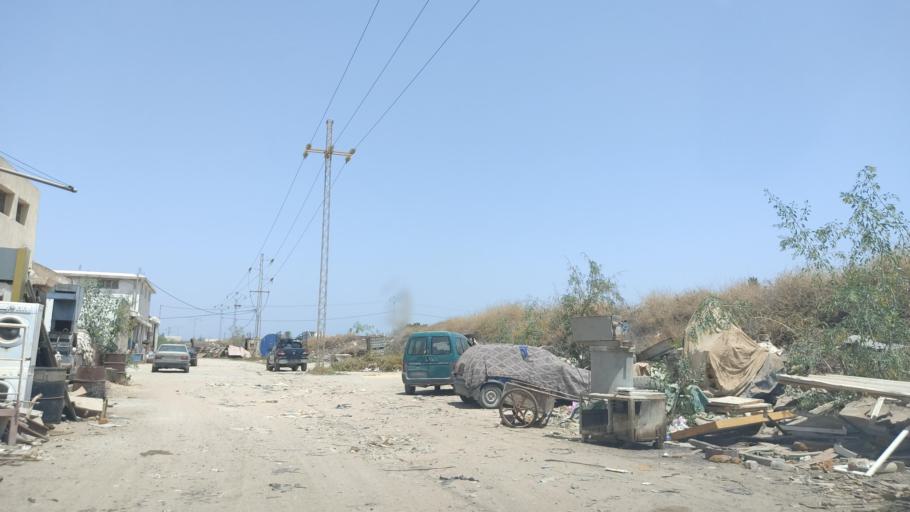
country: TN
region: Safaqis
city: Sfax
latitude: 34.7092
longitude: 10.7305
